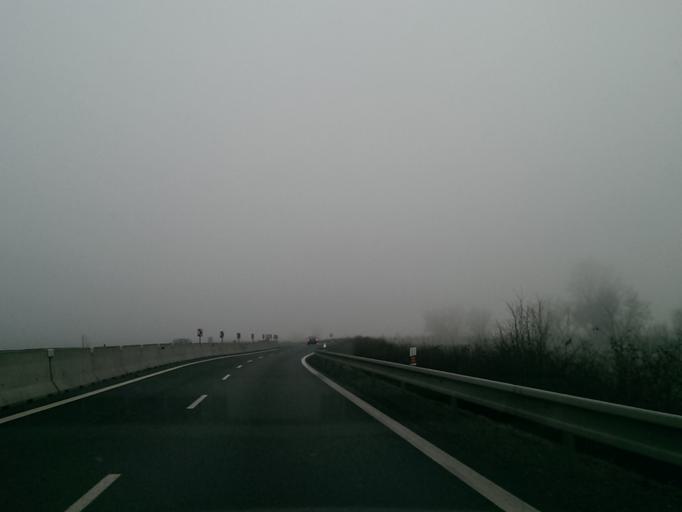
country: CZ
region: Olomoucky
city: Hnevotin
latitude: 49.5975
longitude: 17.1988
